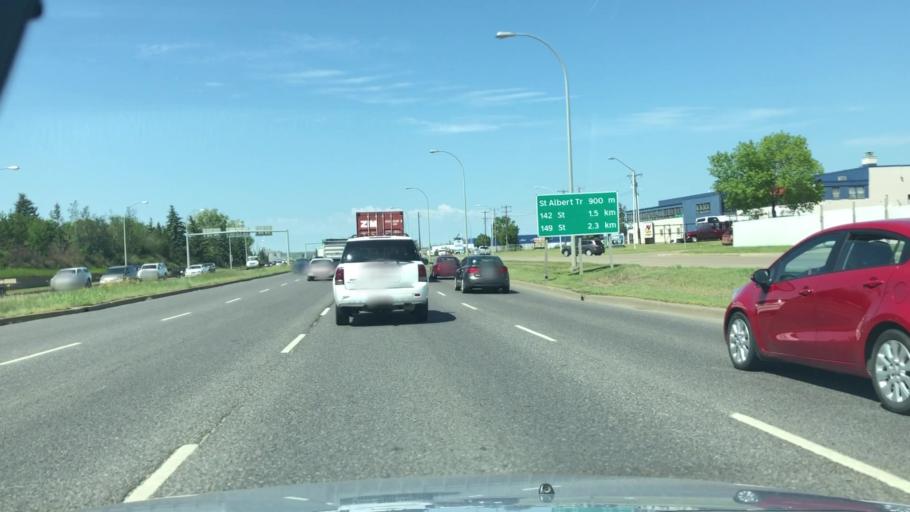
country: CA
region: Alberta
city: Edmonton
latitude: 53.5809
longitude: -113.5436
